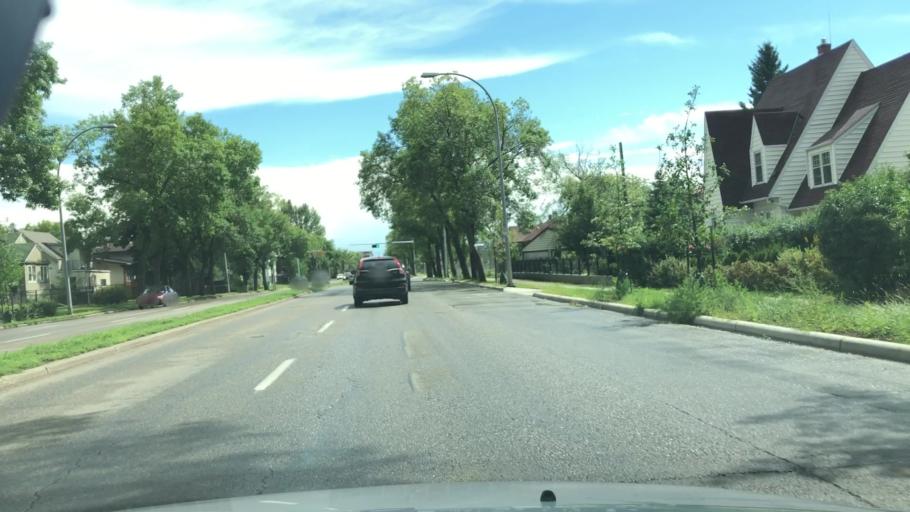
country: CA
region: Alberta
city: Edmonton
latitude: 53.5580
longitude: -113.5085
